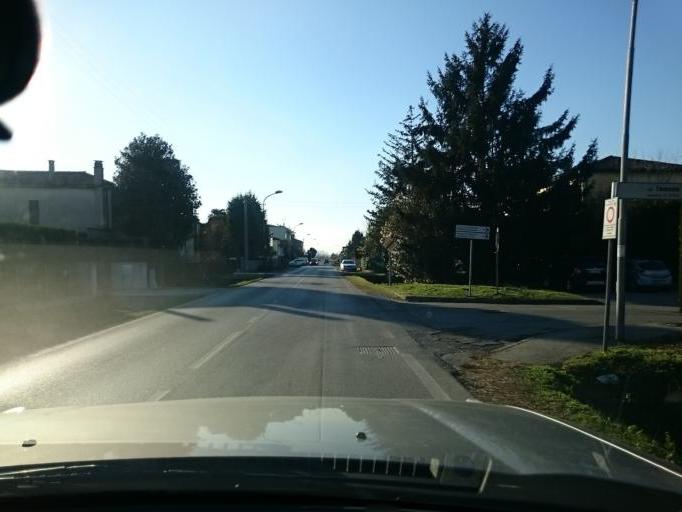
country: IT
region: Veneto
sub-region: Provincia di Venezia
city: Stra
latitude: 45.4044
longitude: 12.0191
